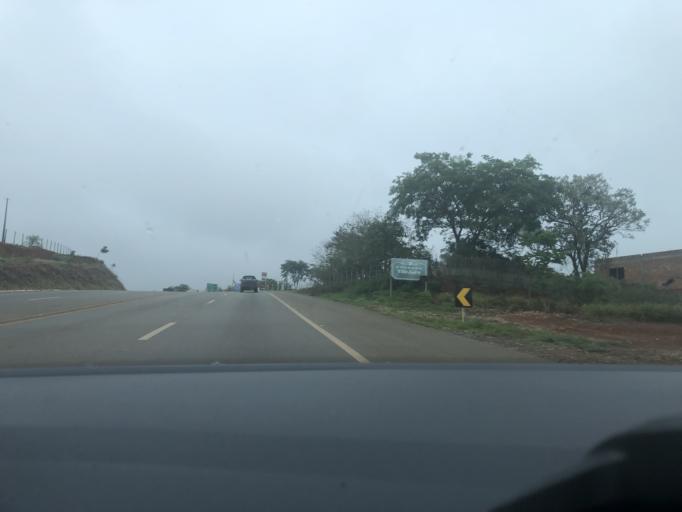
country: BR
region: Minas Gerais
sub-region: Congonhas
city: Congonhas
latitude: -20.6136
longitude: -43.9212
